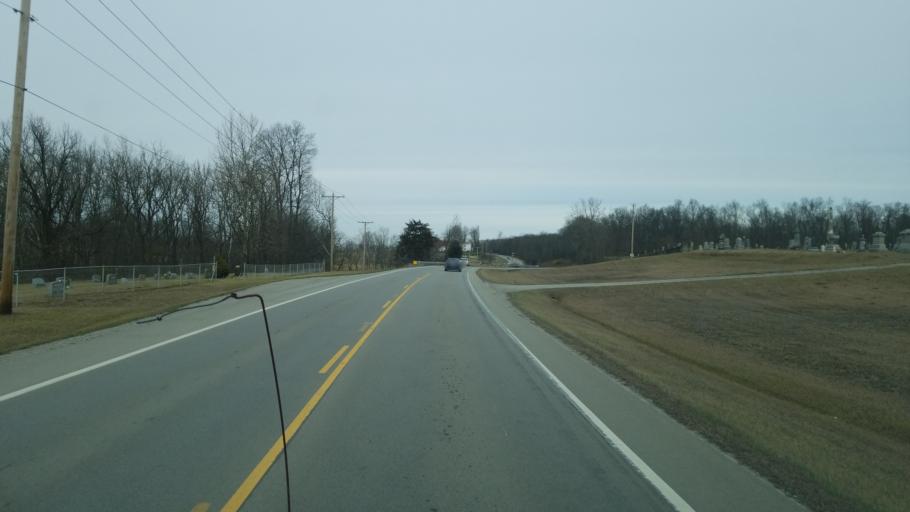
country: US
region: Ohio
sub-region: Adams County
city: Winchester
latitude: 38.9991
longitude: -83.7121
